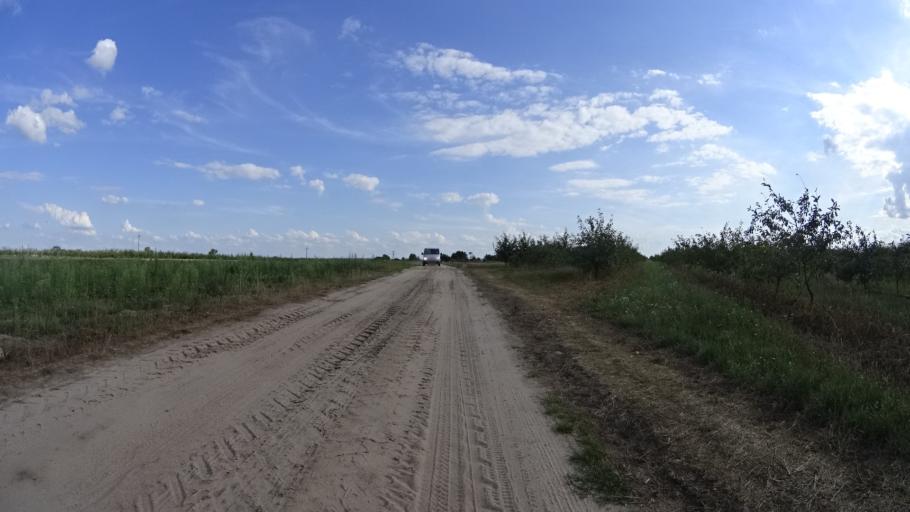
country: PL
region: Masovian Voivodeship
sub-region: Powiat bialobrzeski
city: Wysmierzyce
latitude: 51.6600
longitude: 20.8205
